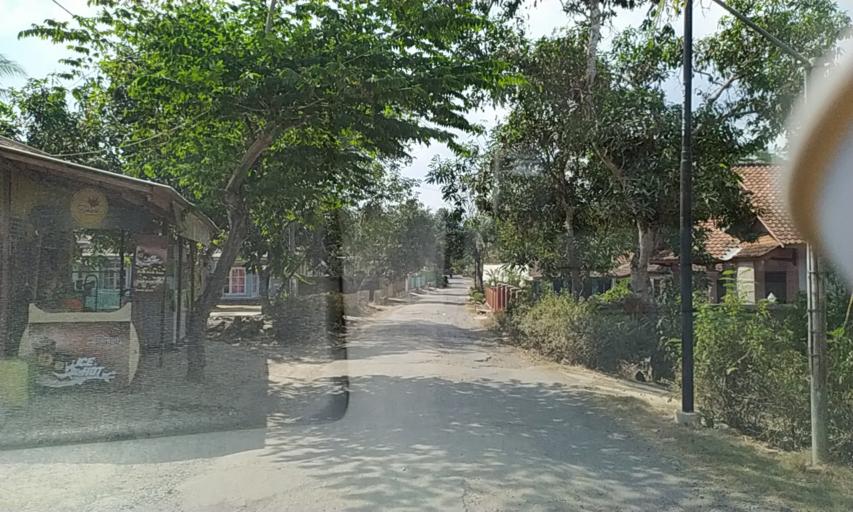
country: ID
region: Central Java
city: Sogati
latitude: -7.3250
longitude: 108.6755
